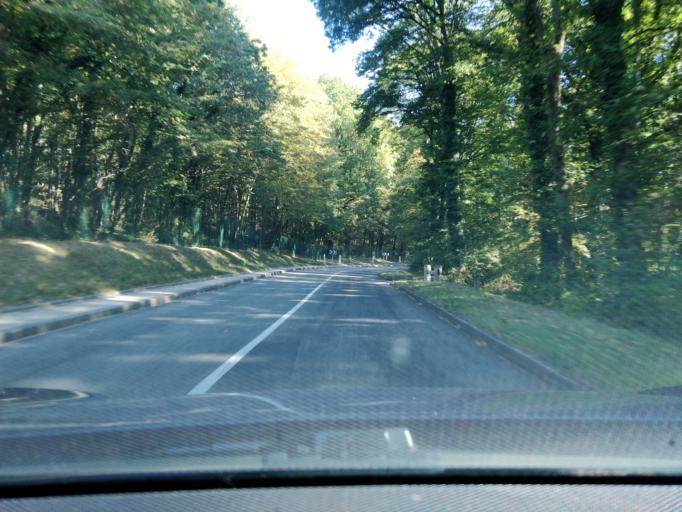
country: FR
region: Ile-de-France
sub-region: Departement de l'Essonne
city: Forges-les-Bains
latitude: 48.6457
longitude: 2.1009
